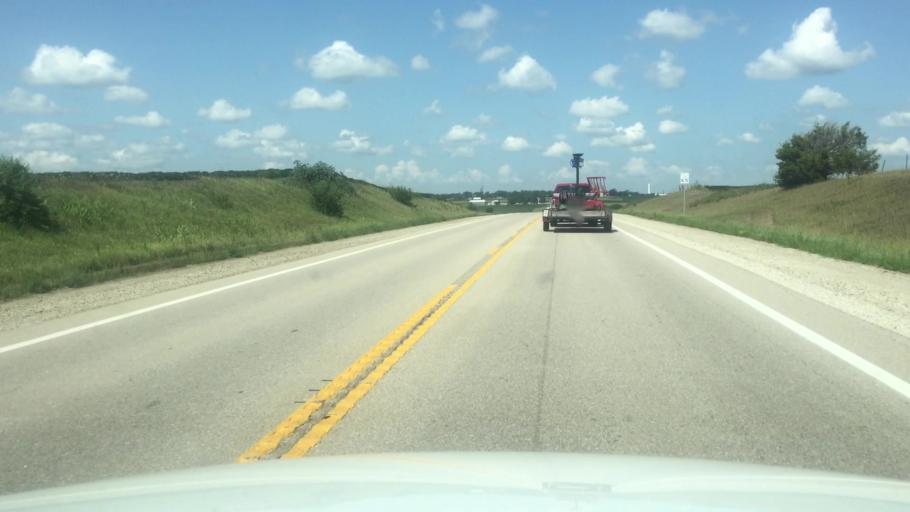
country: US
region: Kansas
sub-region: Nemaha County
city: Sabetha
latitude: 39.8411
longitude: -95.6977
